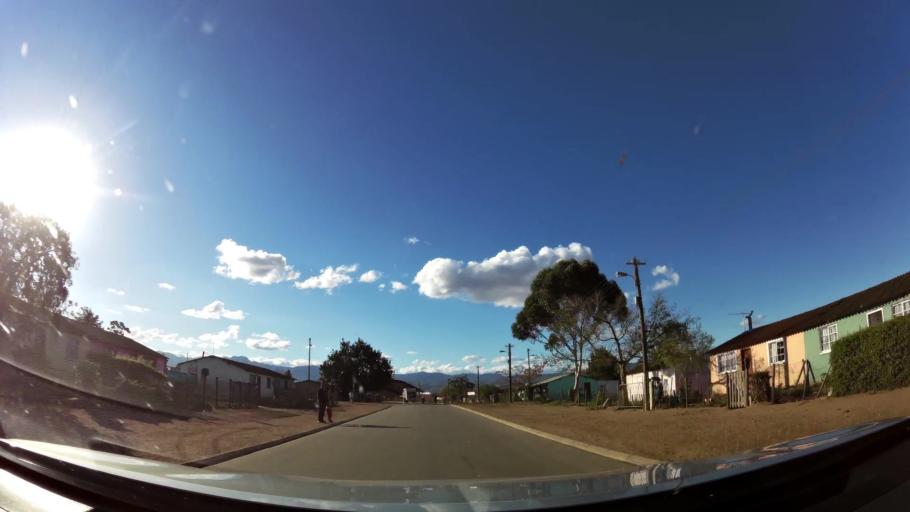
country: ZA
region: Western Cape
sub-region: Eden District Municipality
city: Riversdale
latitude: -34.1052
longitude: 20.9665
